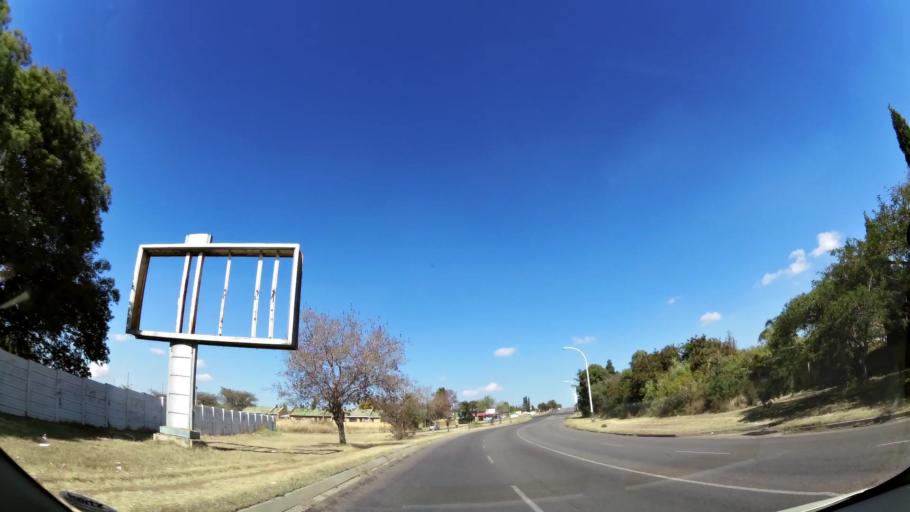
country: ZA
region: Mpumalanga
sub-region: Nkangala District Municipality
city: Witbank
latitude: -25.8658
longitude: 29.2421
